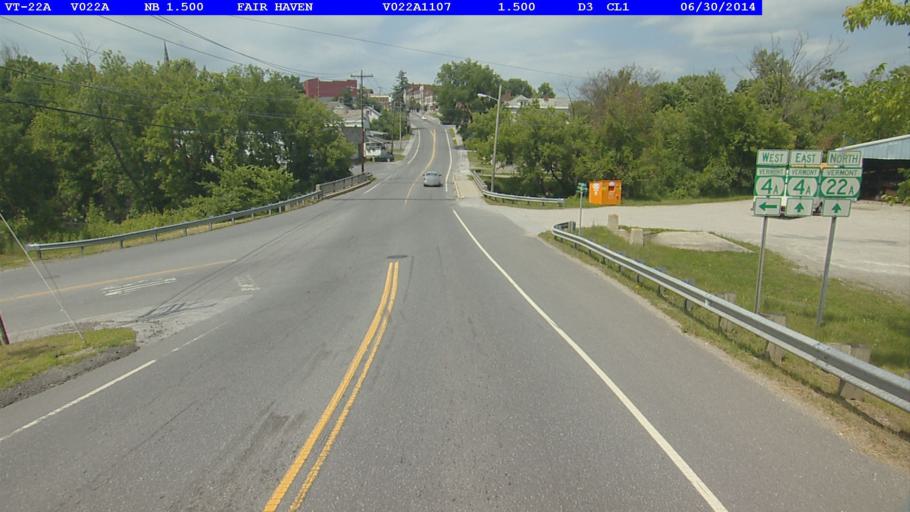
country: US
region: Vermont
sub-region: Rutland County
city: Fair Haven
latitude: 43.5896
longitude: -73.2651
